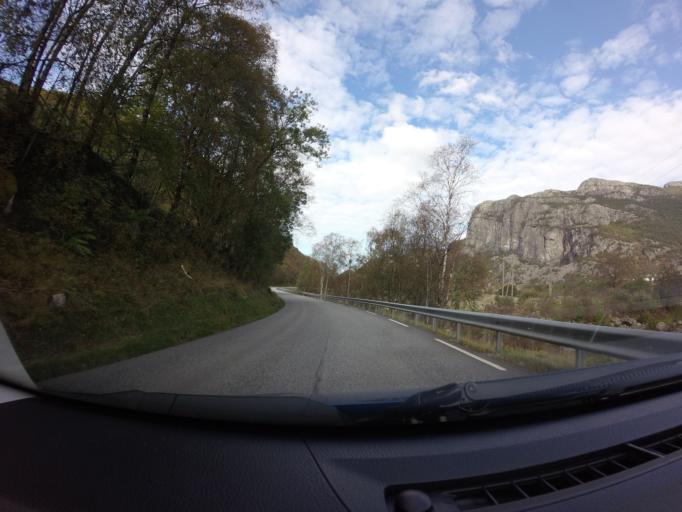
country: NO
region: Rogaland
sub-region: Forsand
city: Forsand
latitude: 58.8019
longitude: 6.2627
